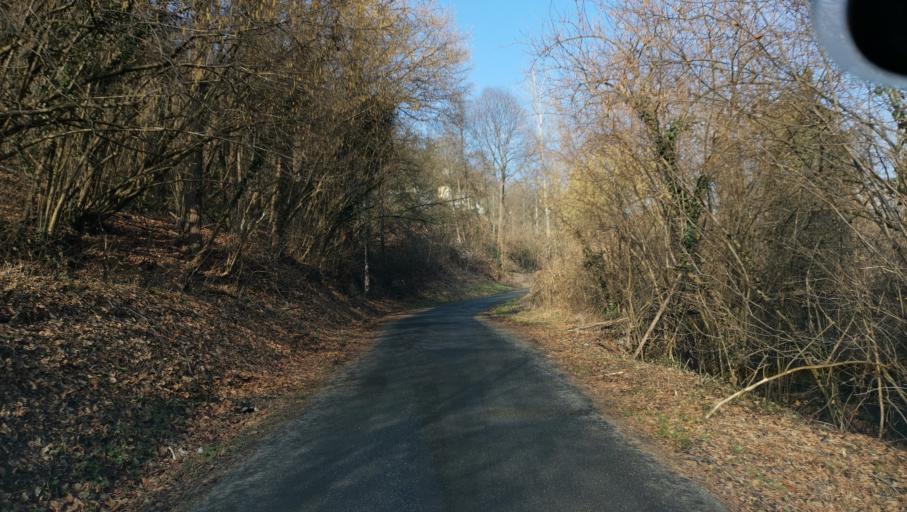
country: IT
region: Piedmont
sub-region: Provincia di Torino
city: San Raffaele Cimena
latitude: 45.1398
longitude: 7.8600
